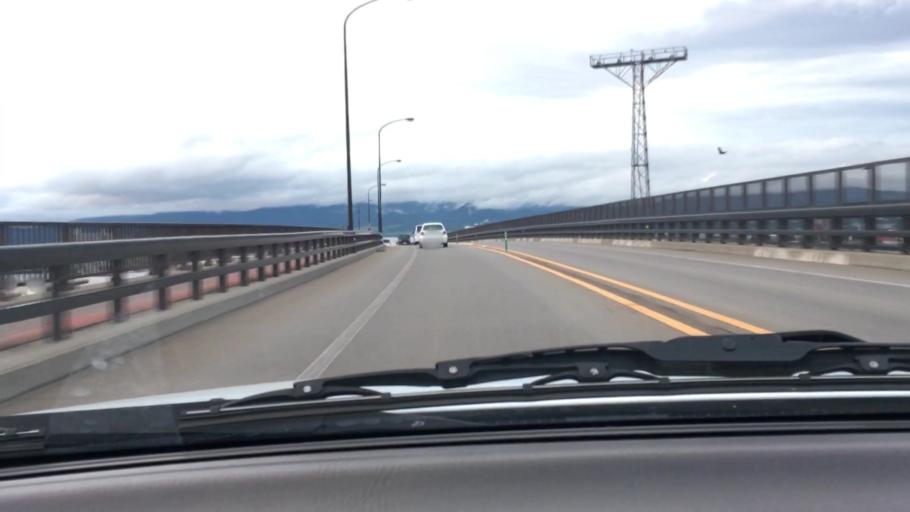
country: JP
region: Hokkaido
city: Hakodate
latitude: 41.7757
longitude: 140.7252
